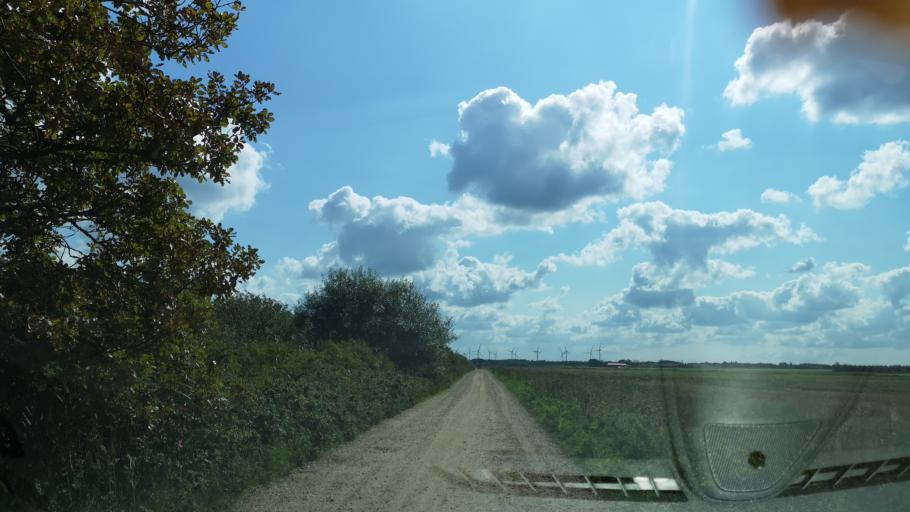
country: DK
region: Central Jutland
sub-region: Ringkobing-Skjern Kommune
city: Skjern
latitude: 55.8994
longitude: 8.3898
